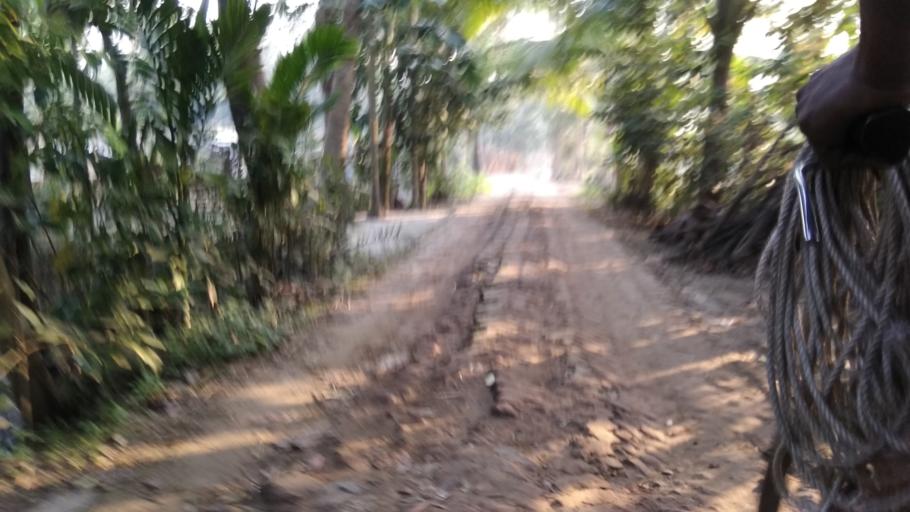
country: BD
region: Barisal
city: Mehendiganj
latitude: 22.9309
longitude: 90.4108
